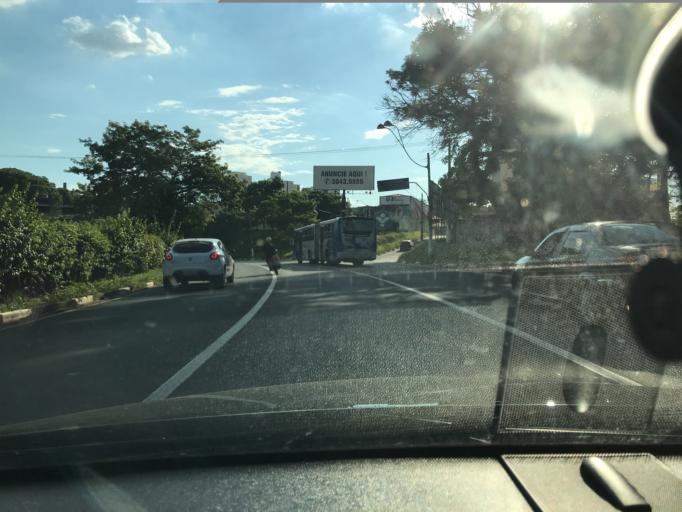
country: BR
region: Sao Paulo
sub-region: Campinas
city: Campinas
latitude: -22.9116
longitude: -47.0583
